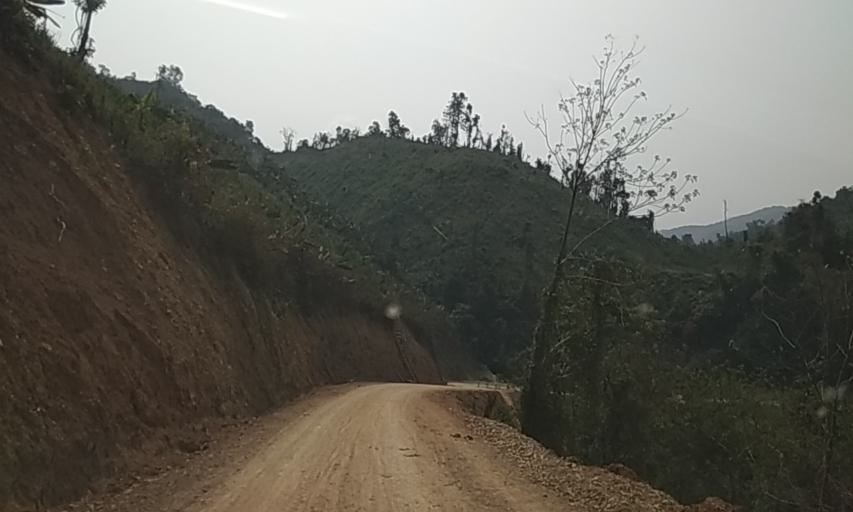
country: LA
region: Phongsali
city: Phongsali
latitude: 21.4695
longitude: 102.4323
